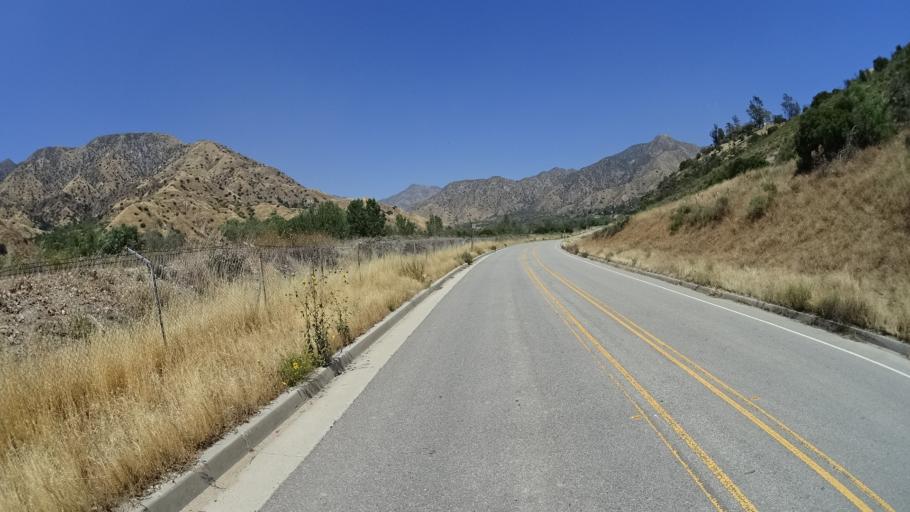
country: US
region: California
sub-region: Los Angeles County
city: La Crescenta-Montrose
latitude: 34.2761
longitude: -118.3092
